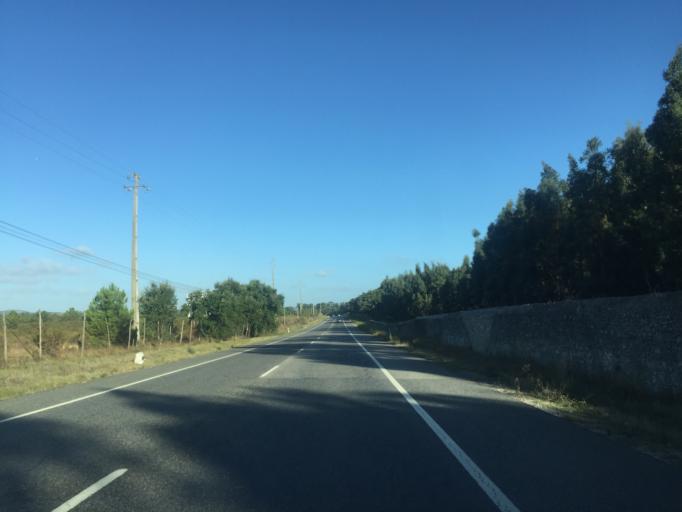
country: PT
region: Lisbon
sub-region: Azambuja
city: Alcoentre
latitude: 39.1778
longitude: -8.9377
